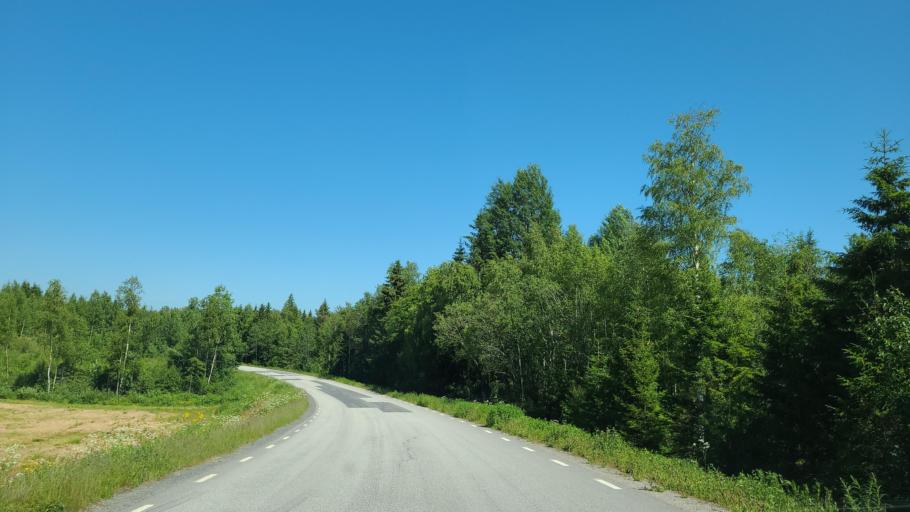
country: SE
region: Vaesternorrland
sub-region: OErnskoeldsviks Kommun
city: Husum
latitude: 63.3909
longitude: 19.2127
